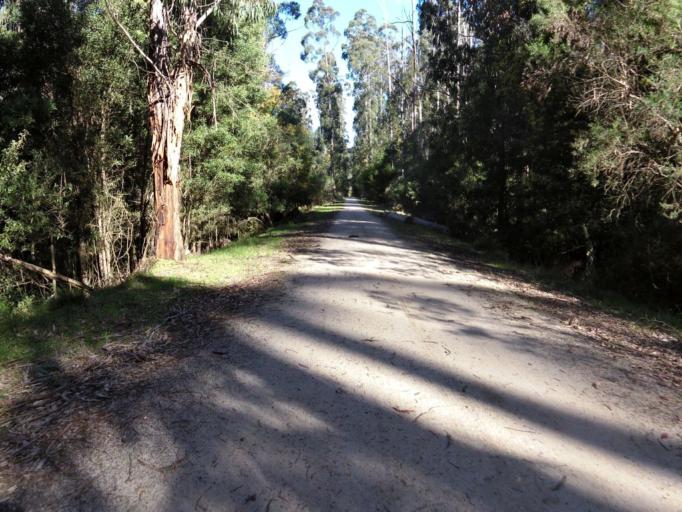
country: AU
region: Victoria
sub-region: Latrobe
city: Moe
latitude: -38.3795
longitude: 146.2416
